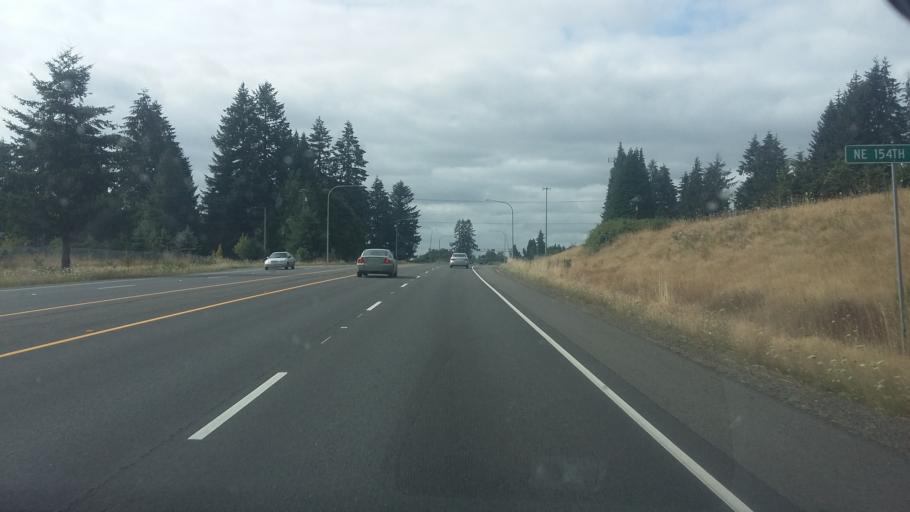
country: US
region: Washington
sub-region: Clark County
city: Brush Prairie
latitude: 45.7350
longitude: -122.5516
